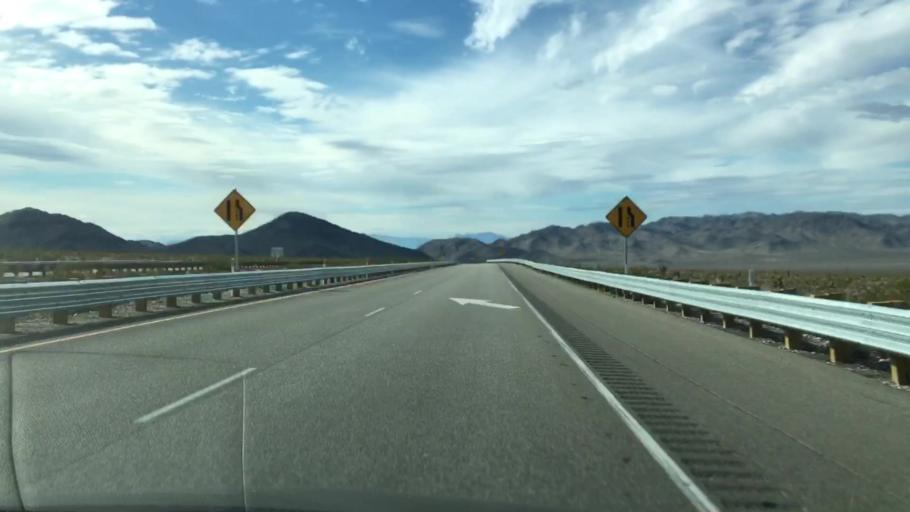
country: US
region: Nevada
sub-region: Nye County
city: Pahrump
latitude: 36.5963
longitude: -116.0086
